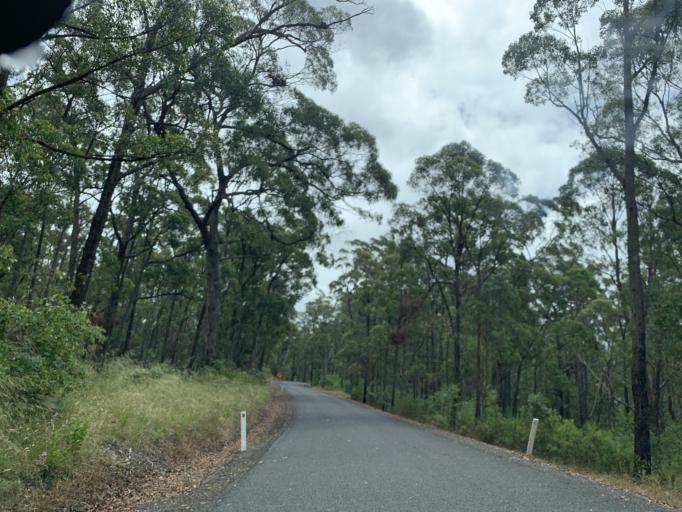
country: AU
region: Victoria
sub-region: Latrobe
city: Traralgon
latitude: -38.1085
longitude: 146.5384
